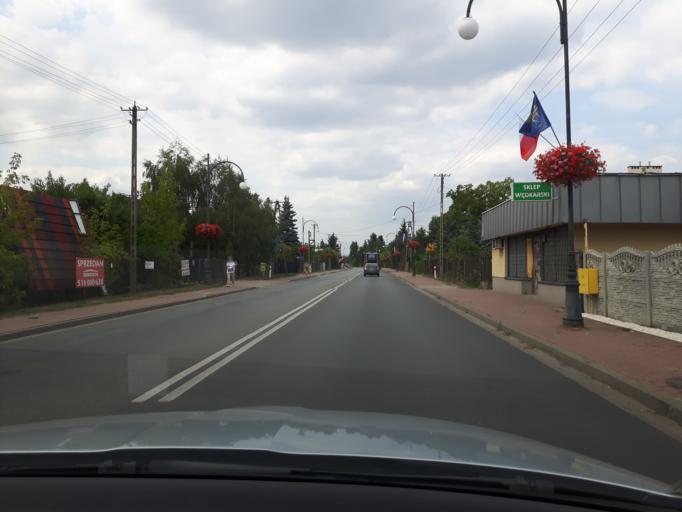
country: PL
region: Masovian Voivodeship
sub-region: Powiat legionowski
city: Nieporet
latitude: 52.4255
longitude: 21.0332
